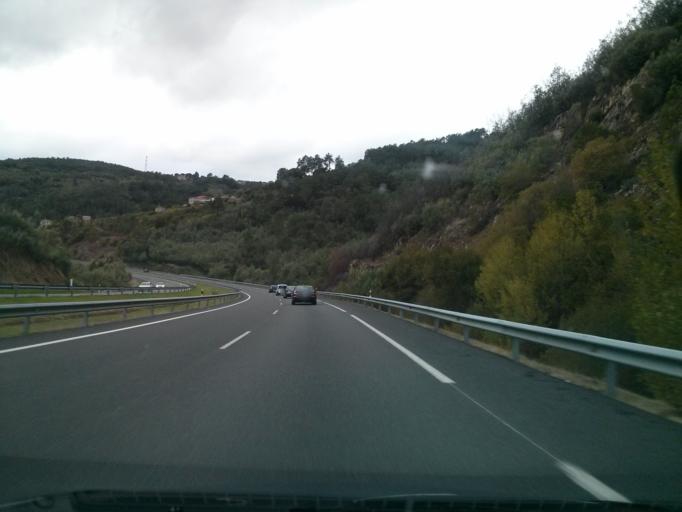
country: ES
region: Galicia
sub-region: Provincia de Ourense
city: Cenlle
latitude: 42.3347
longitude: -8.0645
